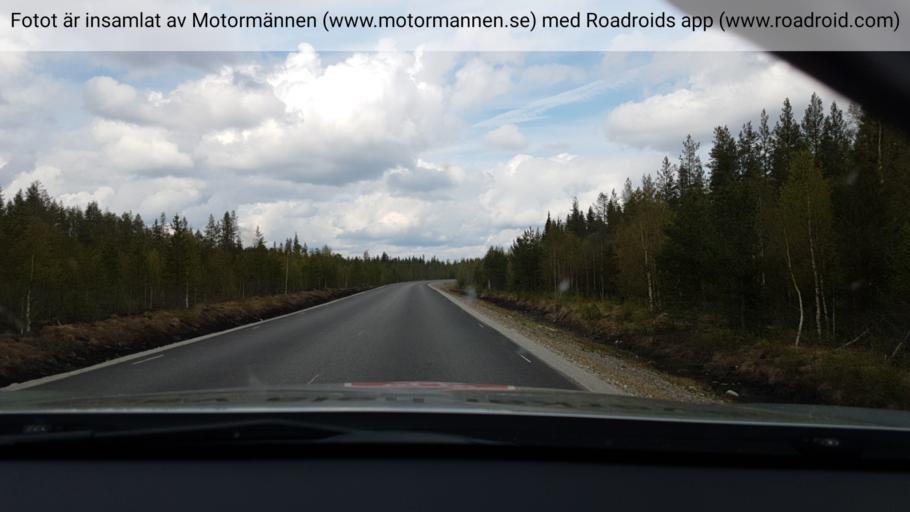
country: SE
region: Vaesterbotten
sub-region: Lycksele Kommun
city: Lycksele
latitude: 64.0289
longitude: 18.4431
